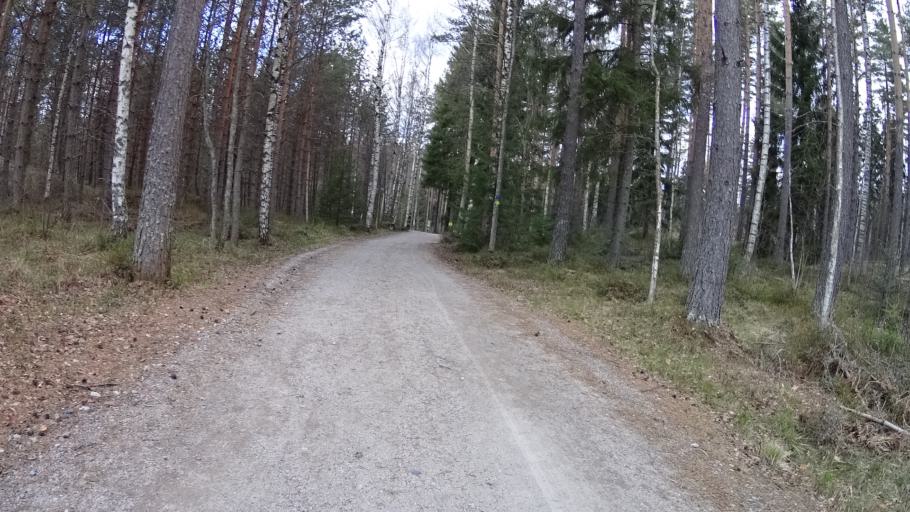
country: FI
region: Uusimaa
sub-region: Helsinki
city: Espoo
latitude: 60.2706
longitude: 24.6359
